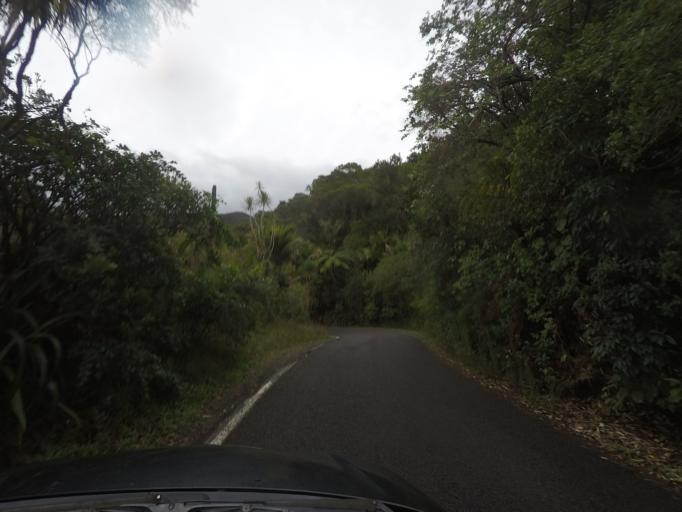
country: NZ
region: Auckland
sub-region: Auckland
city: Muriwai Beach
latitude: -36.9756
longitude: 174.4828
